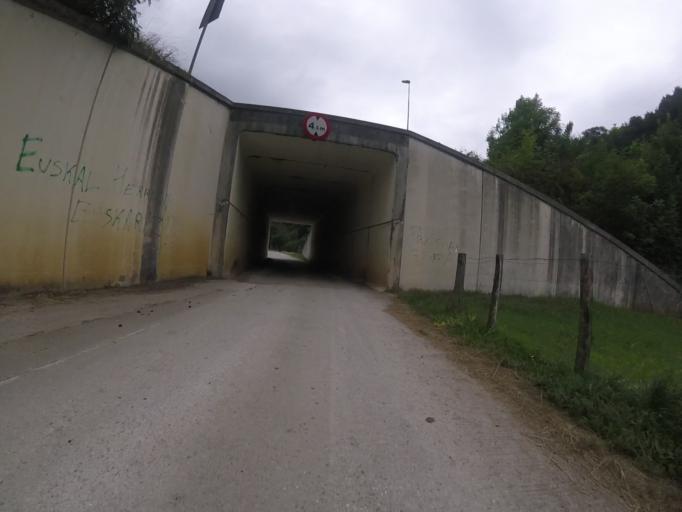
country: ES
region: Navarre
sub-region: Provincia de Navarra
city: Sunbilla
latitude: 43.1855
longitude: -1.6699
